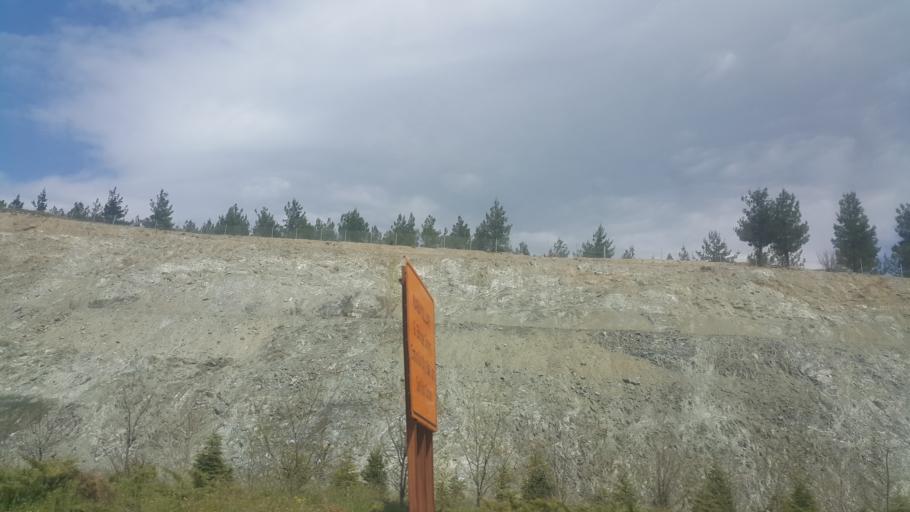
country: TR
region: Adana
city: Pozanti
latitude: 37.4462
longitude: 34.8826
